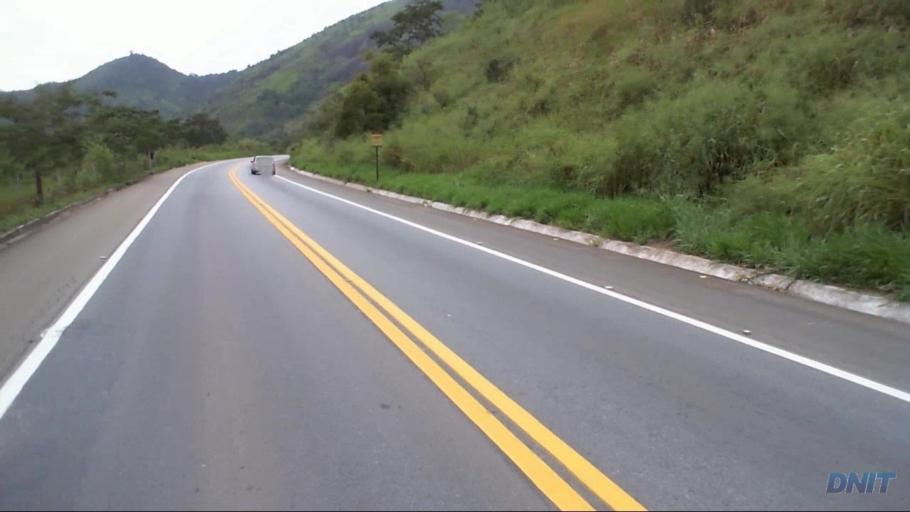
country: BR
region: Minas Gerais
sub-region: Timoteo
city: Timoteo
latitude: -19.5759
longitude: -42.7198
